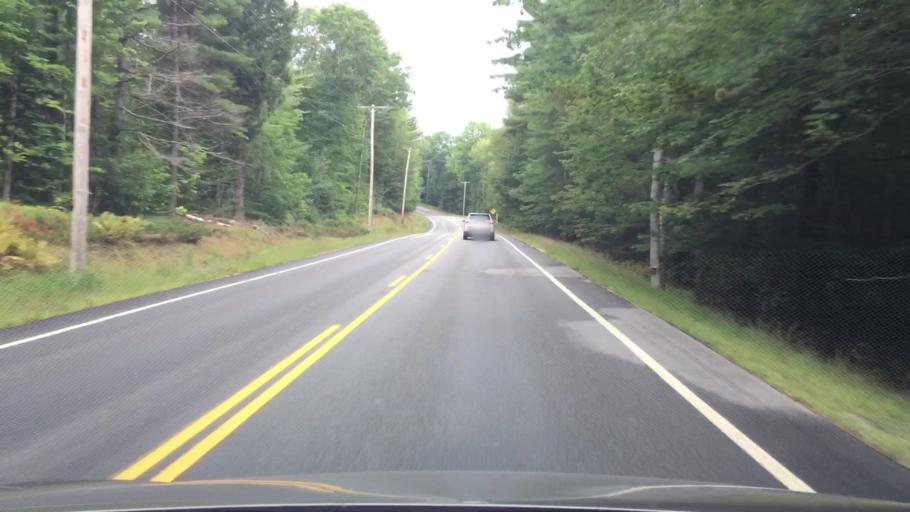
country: US
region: Maine
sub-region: Oxford County
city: Hartford
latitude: 44.3528
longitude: -70.3029
